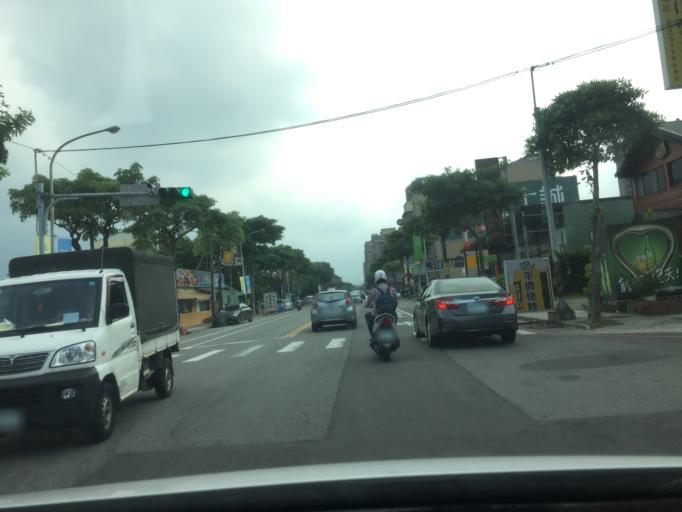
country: TW
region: Taiwan
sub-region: Taoyuan
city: Taoyuan
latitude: 24.9676
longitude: 121.3068
